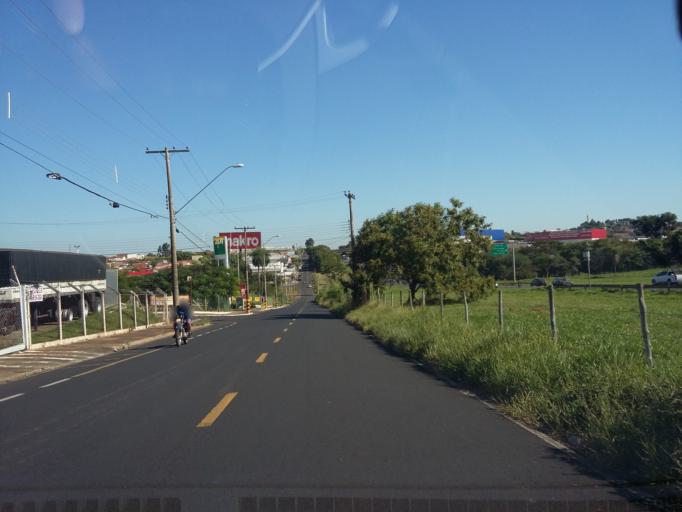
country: BR
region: Sao Paulo
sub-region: Sao Jose Do Rio Preto
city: Sao Jose do Rio Preto
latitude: -20.8359
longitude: -49.3655
